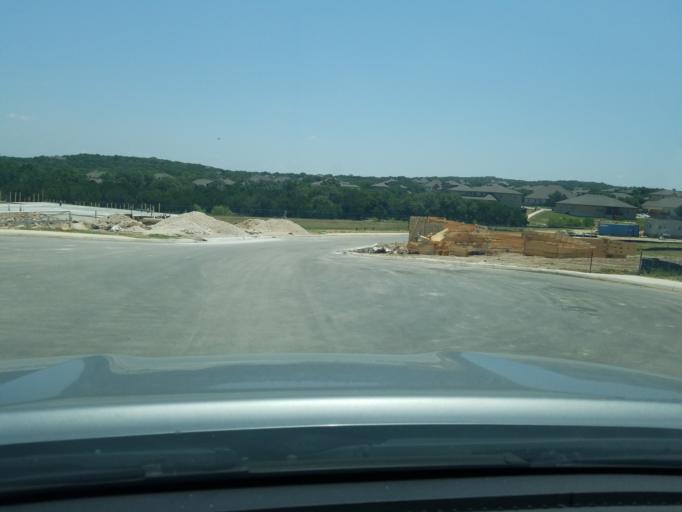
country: US
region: Texas
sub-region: Bexar County
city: Timberwood Park
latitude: 29.7153
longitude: -98.5113
